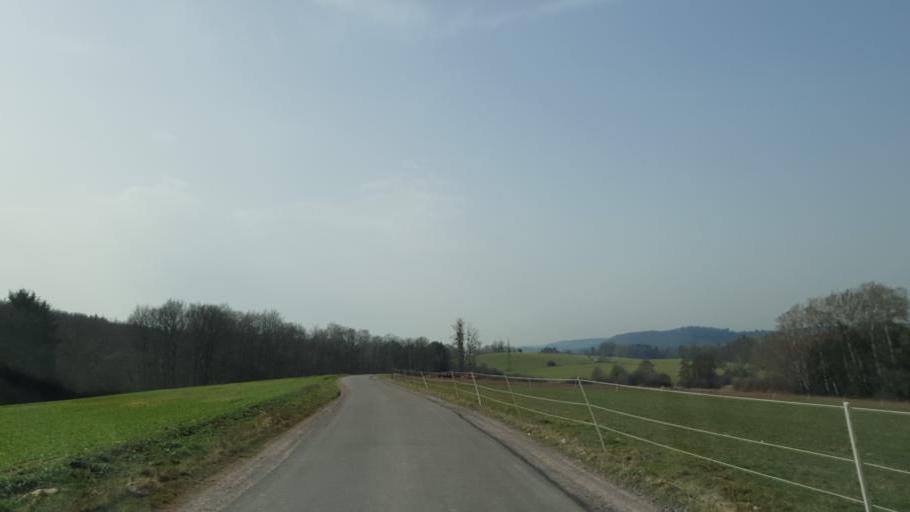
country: DE
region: Saarland
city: Nalbach
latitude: 49.4311
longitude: 6.7896
